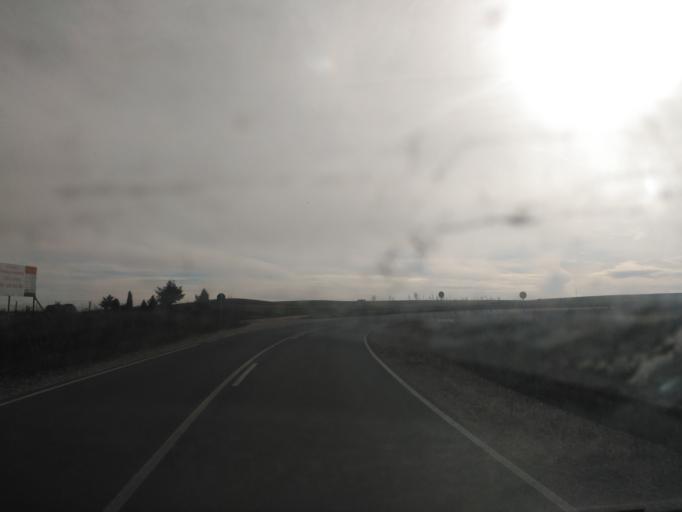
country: ES
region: Castille and Leon
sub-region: Provincia de Salamanca
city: Moriscos
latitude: 41.0063
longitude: -5.5832
